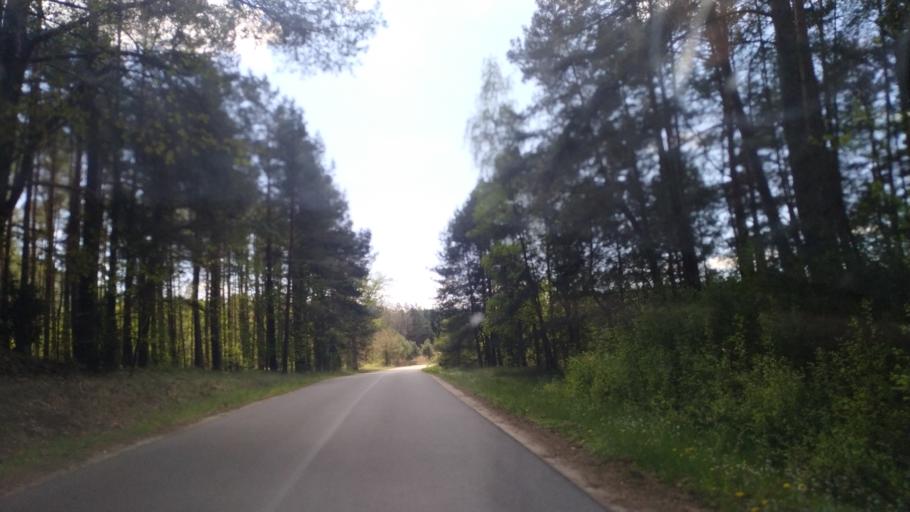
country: PL
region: Greater Poland Voivodeship
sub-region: Powiat pilski
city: Pila
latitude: 53.2456
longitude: 16.7089
